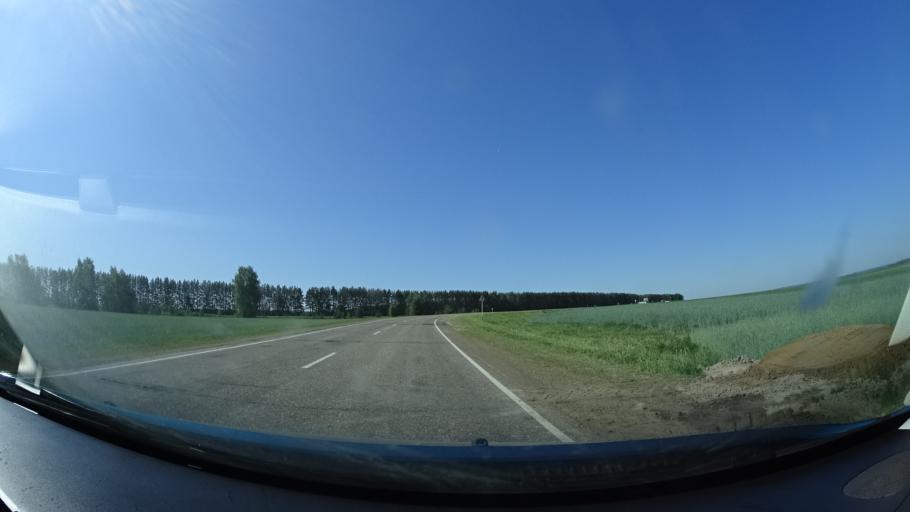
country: RU
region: Bashkortostan
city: Starobaltachevo
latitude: 55.9354
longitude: 55.8271
